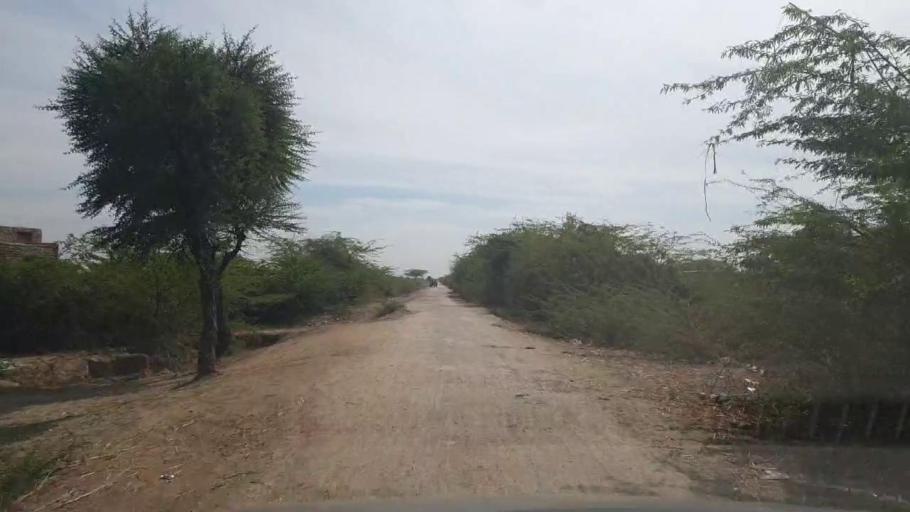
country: PK
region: Sindh
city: Kunri
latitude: 25.3055
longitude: 69.5742
